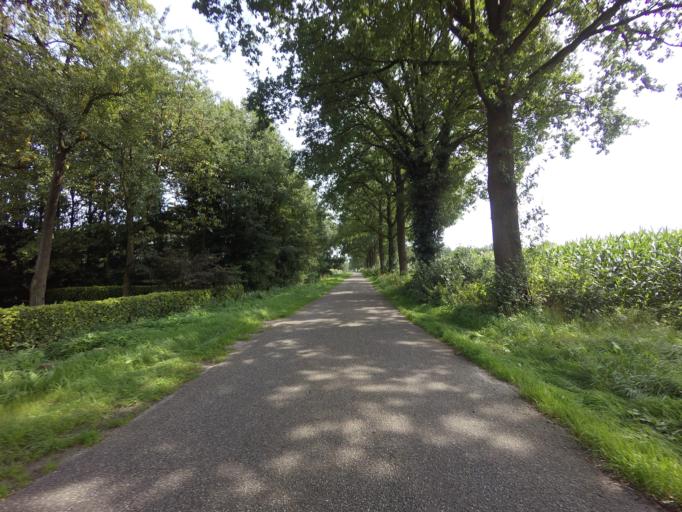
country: DE
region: Lower Saxony
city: Lage
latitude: 52.3968
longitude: 6.9304
